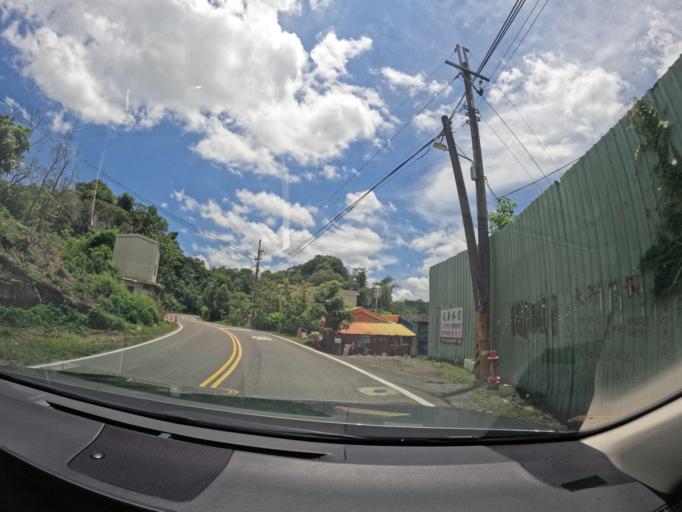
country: TW
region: Taiwan
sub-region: Hsinchu
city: Hsinchu
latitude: 24.6453
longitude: 120.9664
